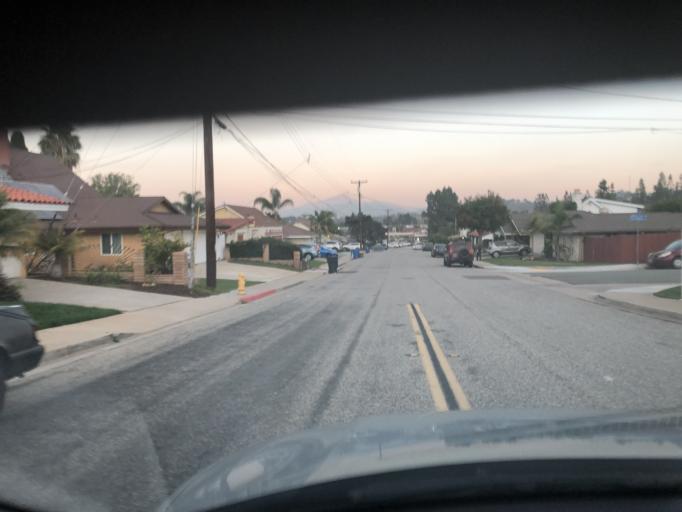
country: US
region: California
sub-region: San Diego County
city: Chula Vista
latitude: 32.6467
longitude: -117.0680
